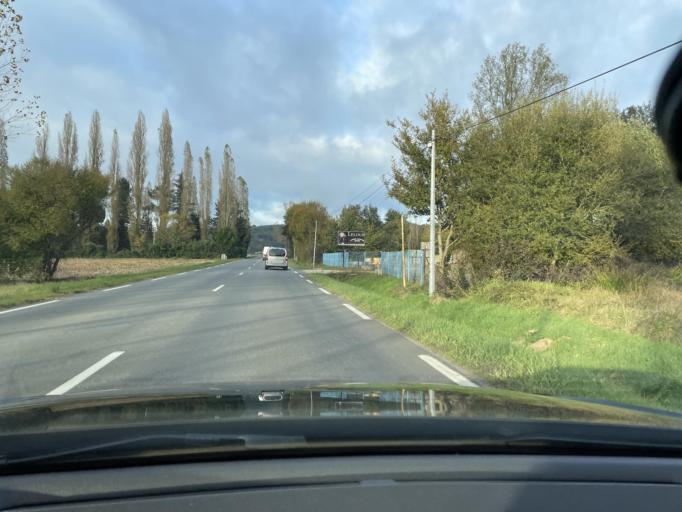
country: FR
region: Aquitaine
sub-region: Departement du Lot-et-Garonne
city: Casteljaloux
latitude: 44.3386
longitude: 0.1047
